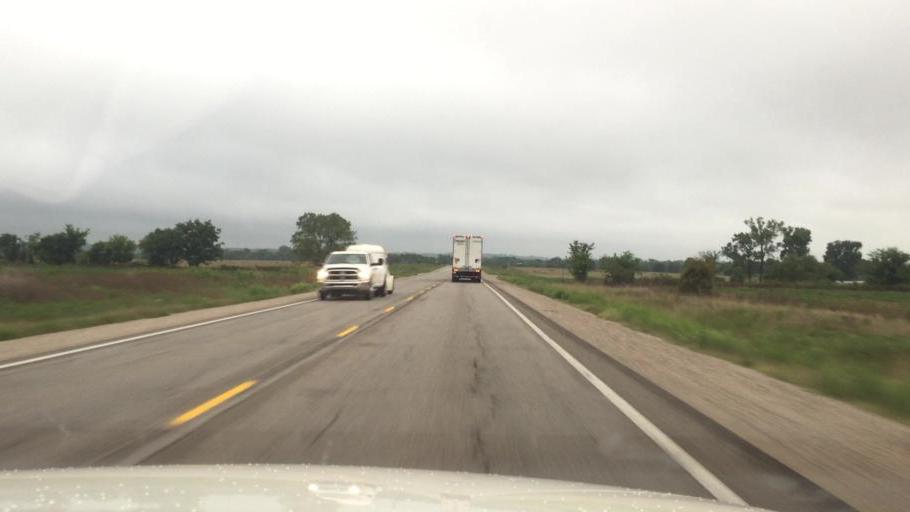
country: US
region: Kansas
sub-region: Montgomery County
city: Cherryvale
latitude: 37.1960
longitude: -95.5821
